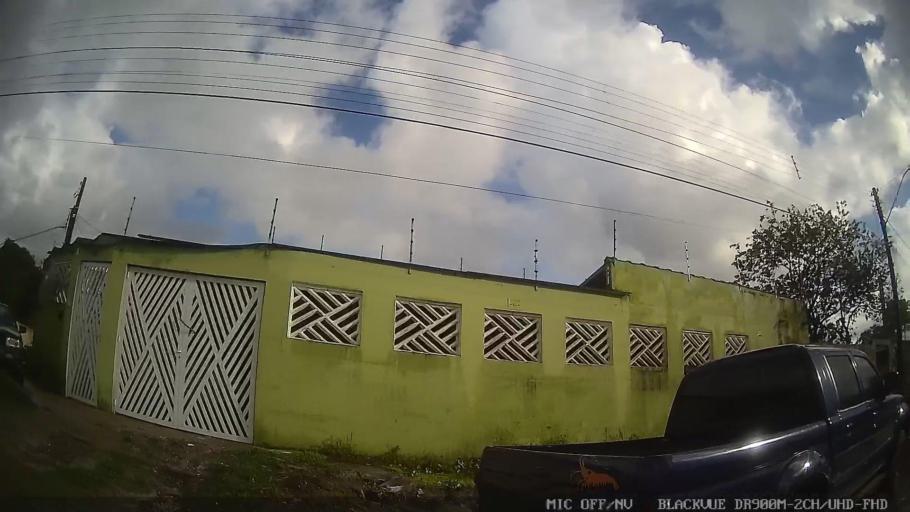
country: BR
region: Sao Paulo
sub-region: Itanhaem
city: Itanhaem
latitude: -24.1742
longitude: -46.8494
